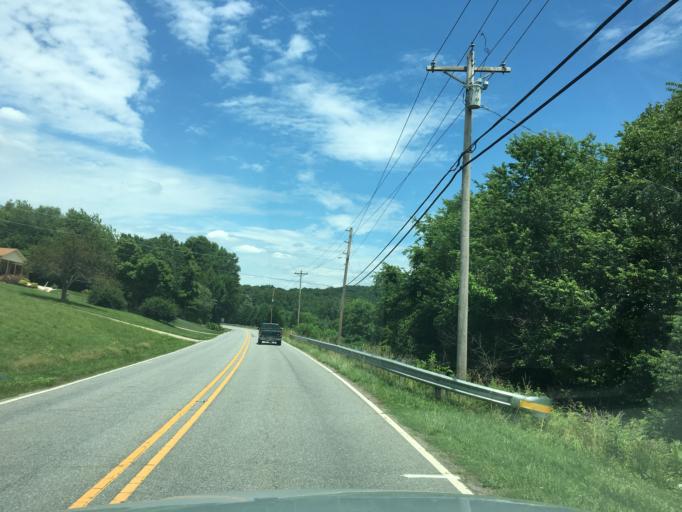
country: US
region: North Carolina
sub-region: Burke County
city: Glen Alpine
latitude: 35.7035
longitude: -81.7609
